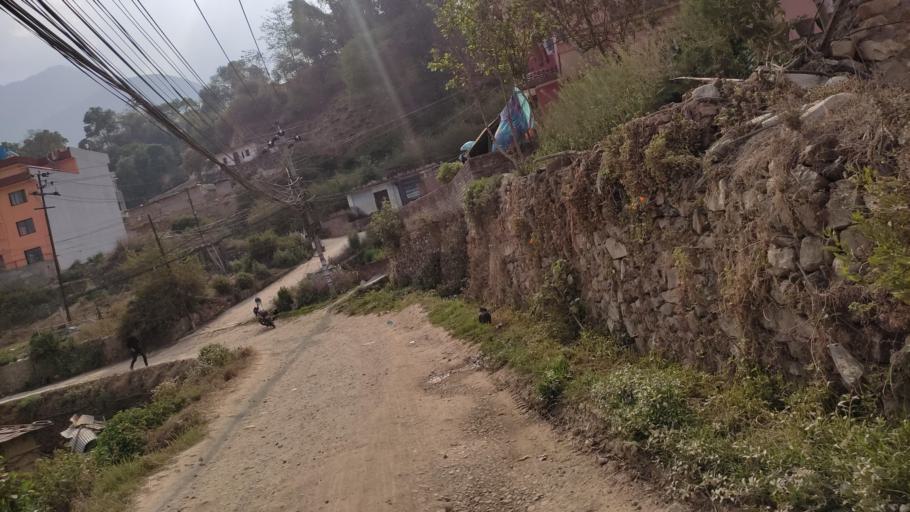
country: NP
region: Central Region
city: Kirtipur
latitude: 27.6643
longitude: 85.2582
